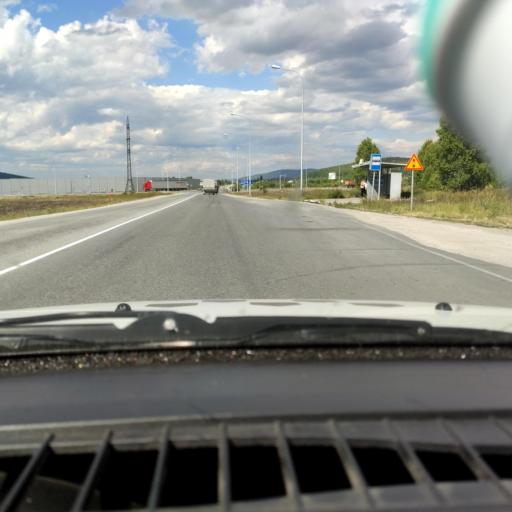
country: RU
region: Chelyabinsk
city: Miass
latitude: 54.9425
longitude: 60.0499
